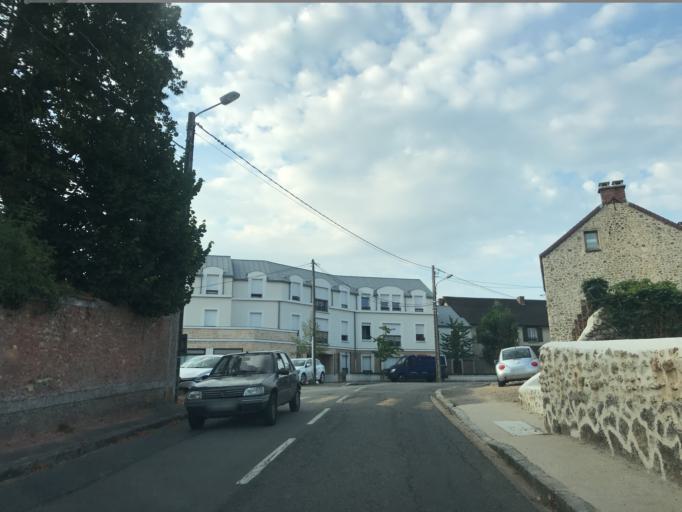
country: FR
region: Ile-de-France
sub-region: Departement des Yvelines
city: Jouars-Pontchartrain
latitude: 48.7561
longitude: 1.8817
